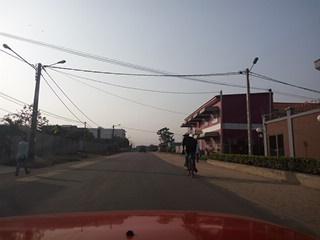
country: CI
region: Lagunes
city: Abobo
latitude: 5.3941
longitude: -3.9822
